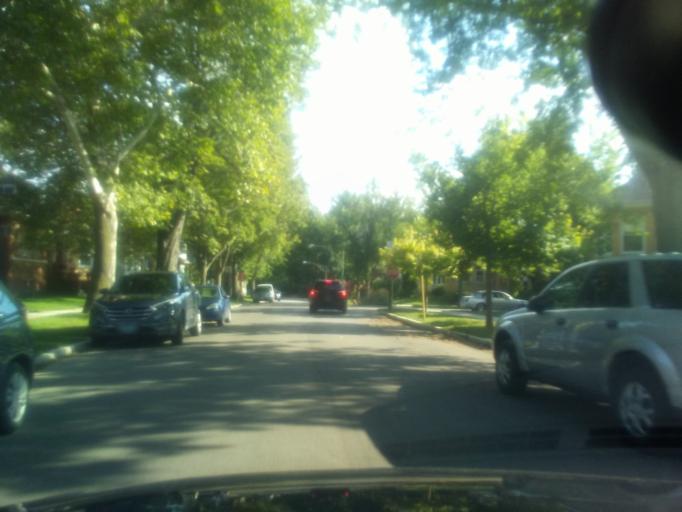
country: US
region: Illinois
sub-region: Cook County
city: Lincolnwood
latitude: 41.9742
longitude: -87.7172
